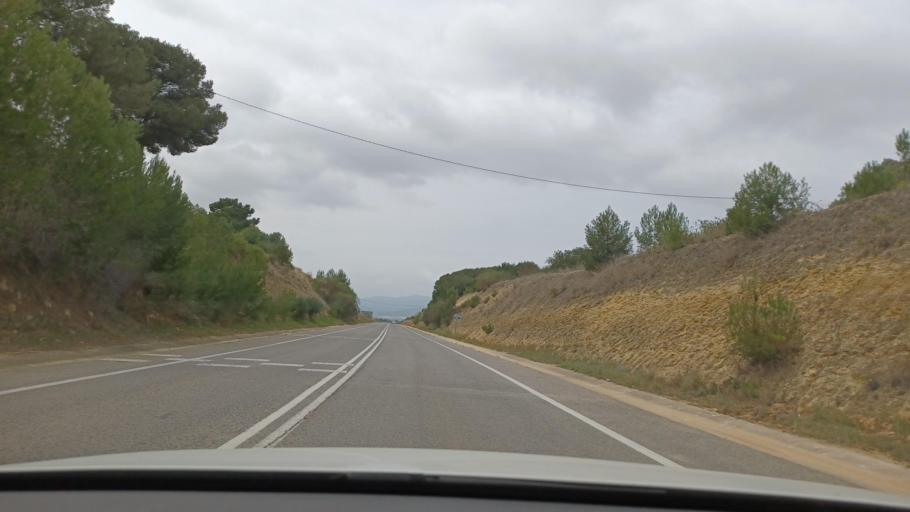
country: ES
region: Catalonia
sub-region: Provincia de Tarragona
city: La Secuita
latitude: 41.1965
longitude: 1.2610
